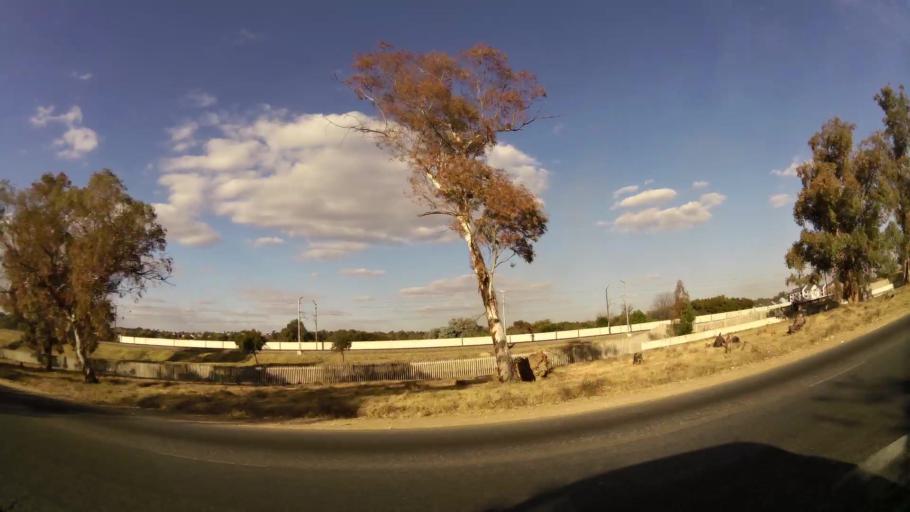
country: ZA
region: Gauteng
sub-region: City of Johannesburg Metropolitan Municipality
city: Midrand
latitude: -25.9597
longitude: 28.1395
